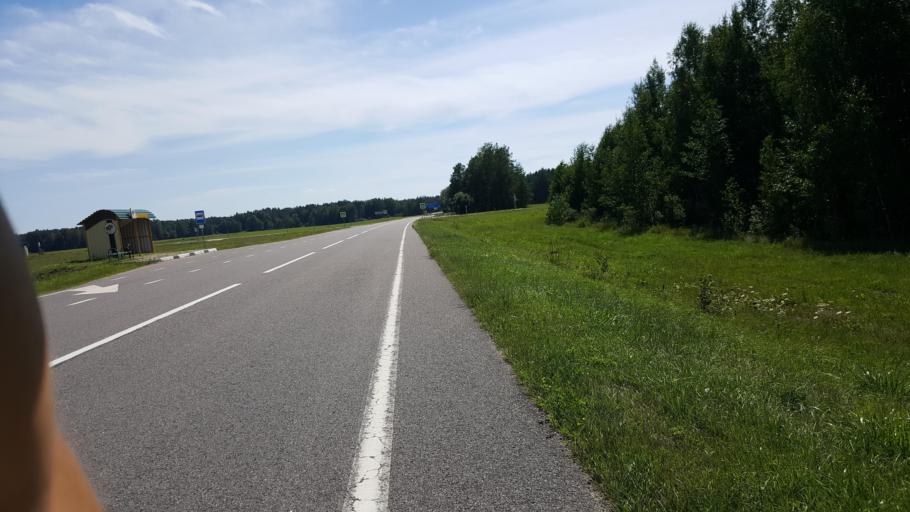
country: BY
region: Brest
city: Zhabinka
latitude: 52.4611
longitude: 24.1422
